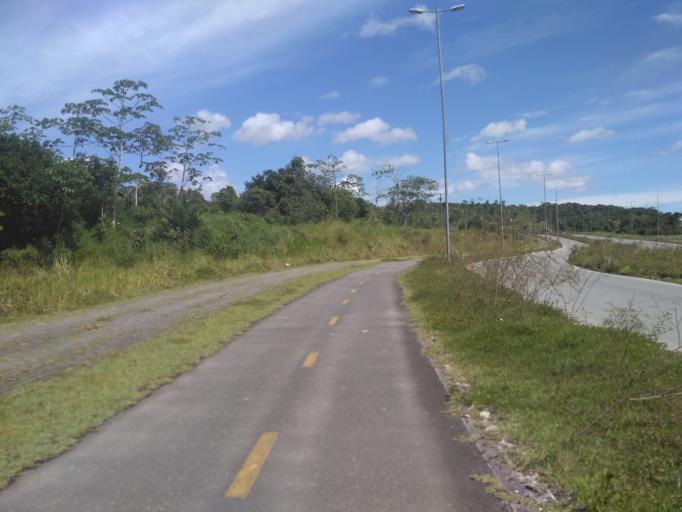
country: BR
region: Pernambuco
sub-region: Sao Lourenco Da Mata
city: Sao Lourenco da Mata
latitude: -8.0443
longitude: -34.9986
